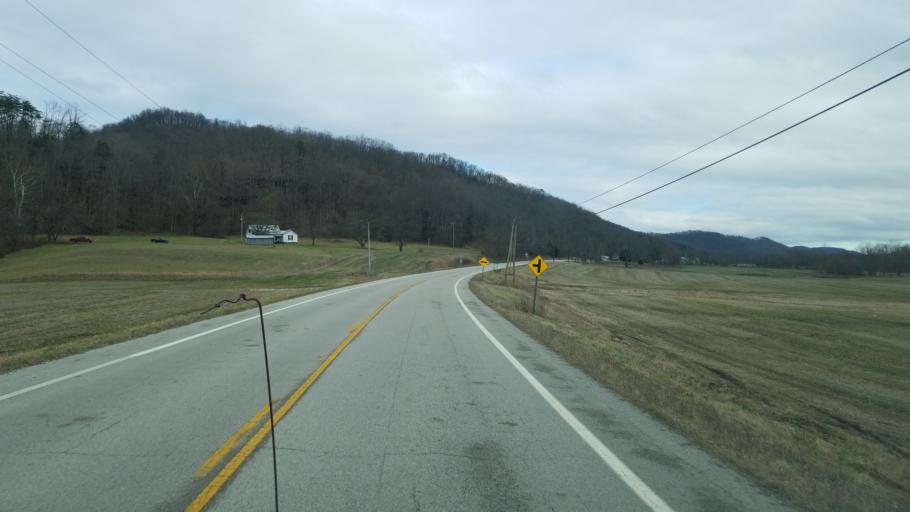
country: US
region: Kentucky
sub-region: Lewis County
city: Vanceburg
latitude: 38.6685
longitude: -83.3829
